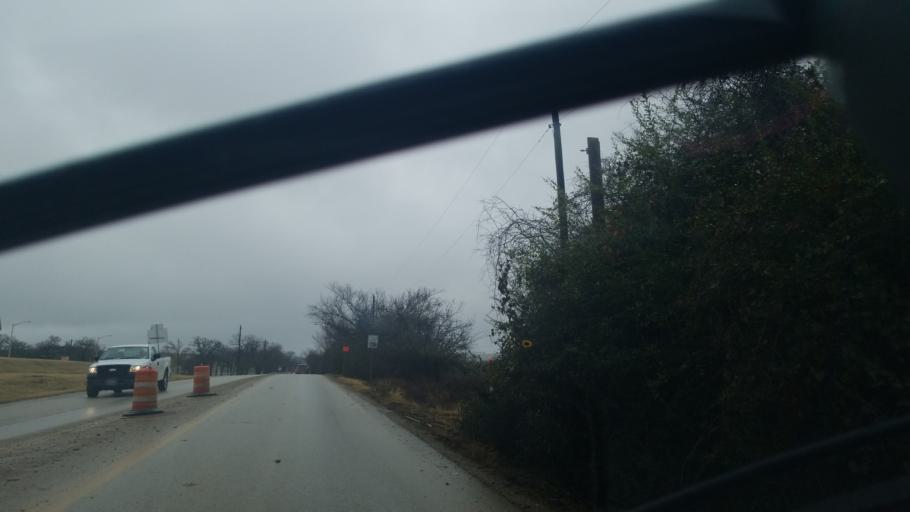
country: US
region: Texas
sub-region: Denton County
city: Corinth
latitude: 33.1947
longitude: -97.0848
